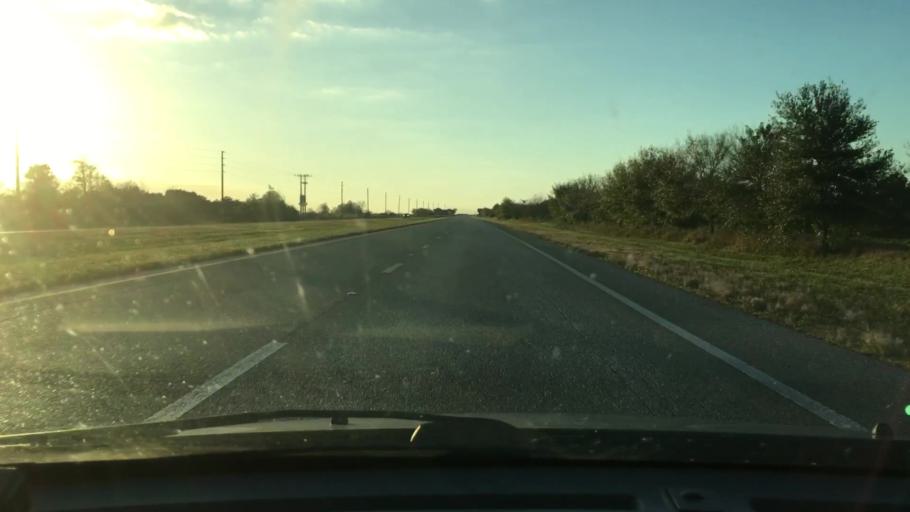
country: US
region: Florida
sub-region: Indian River County
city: Fellsmere
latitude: 27.6409
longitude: -80.6663
